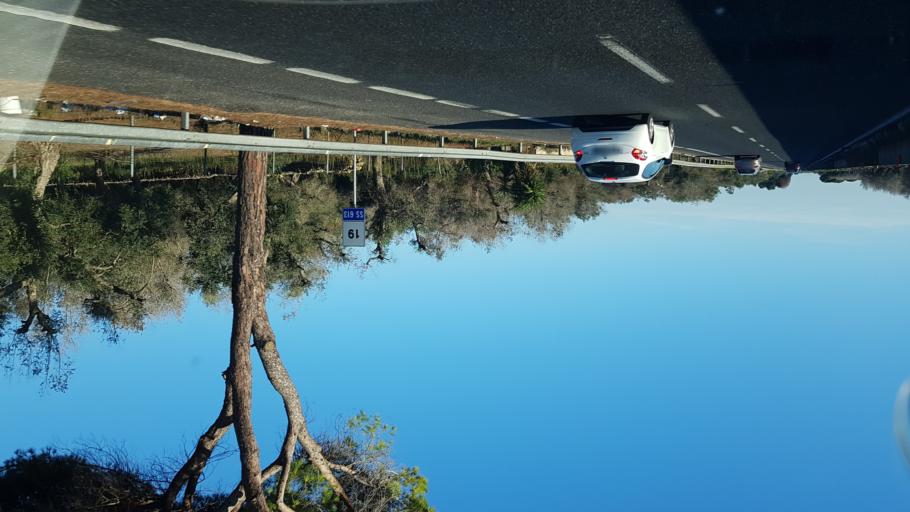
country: IT
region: Apulia
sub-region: Provincia di Brindisi
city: Torchiarolo
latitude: 40.4703
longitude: 18.0513
